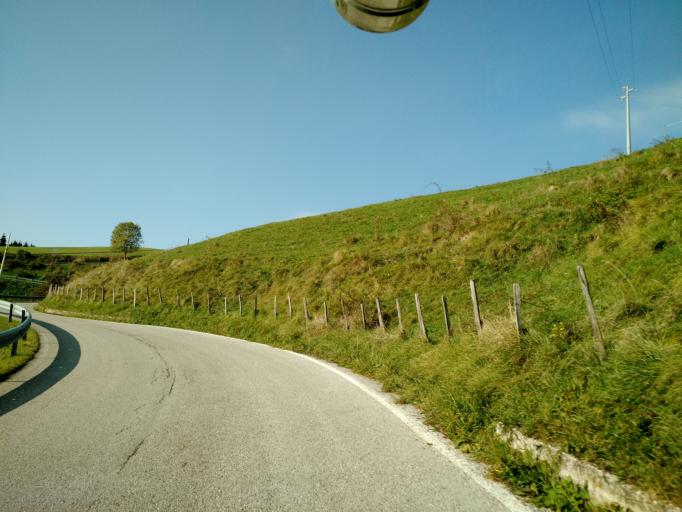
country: IT
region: Veneto
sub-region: Provincia di Vicenza
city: Foza
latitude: 45.8918
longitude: 11.5829
